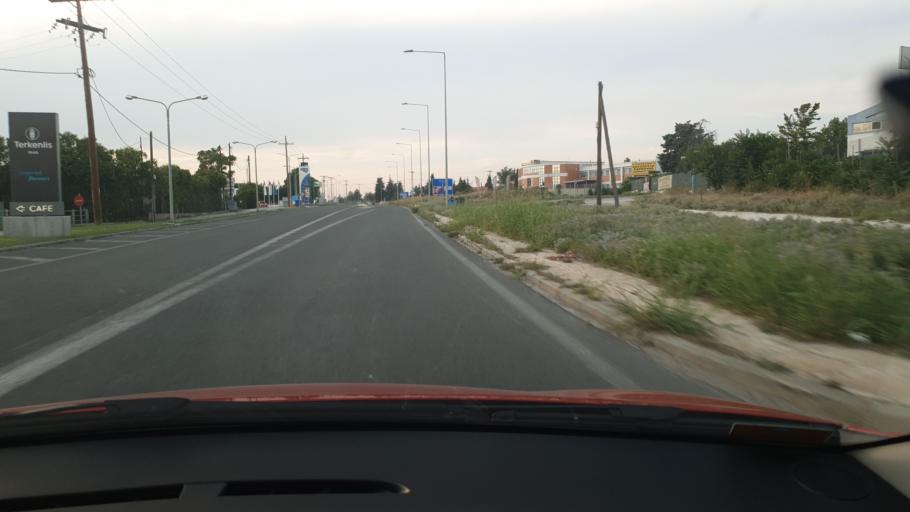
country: GR
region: Central Macedonia
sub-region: Nomos Thessalonikis
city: Thermi
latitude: 40.5312
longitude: 23.0416
